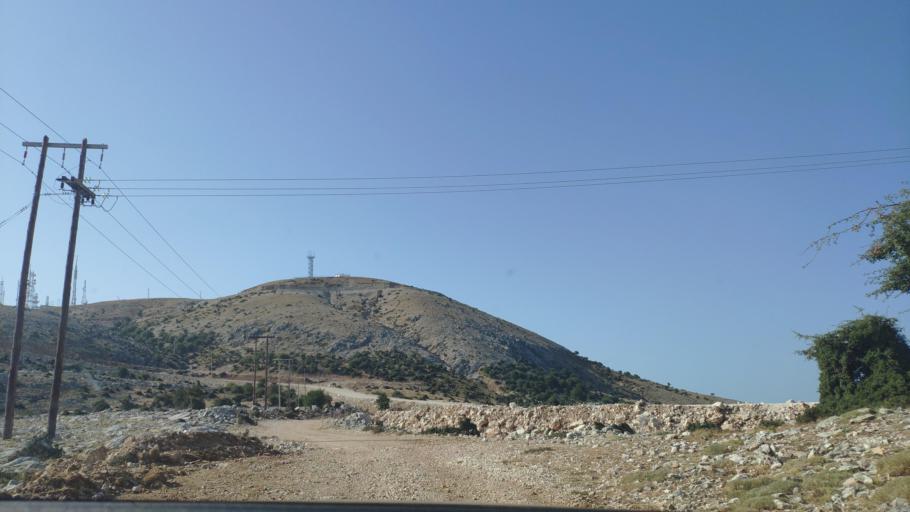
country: GR
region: West Greece
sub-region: Nomos Aitolias kai Akarnanias
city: Monastirakion
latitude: 38.8151
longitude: 20.9791
